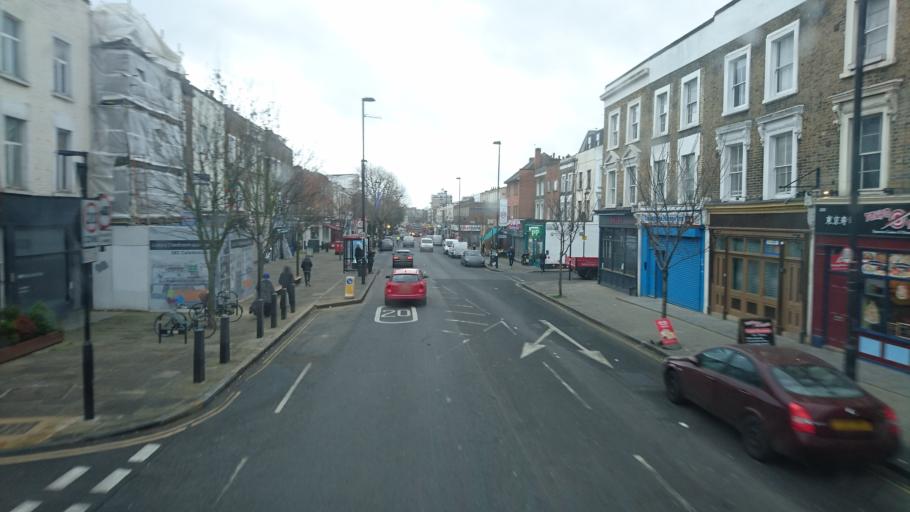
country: GB
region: England
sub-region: Greater London
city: Barnsbury
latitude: 51.5423
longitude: -0.1173
